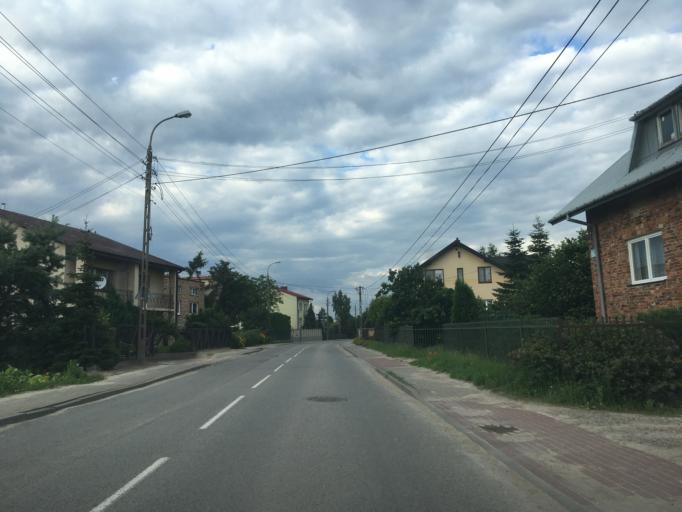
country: PL
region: Masovian Voivodeship
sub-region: Powiat piaseczynski
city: Mysiadlo
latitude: 52.1074
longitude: 20.9796
